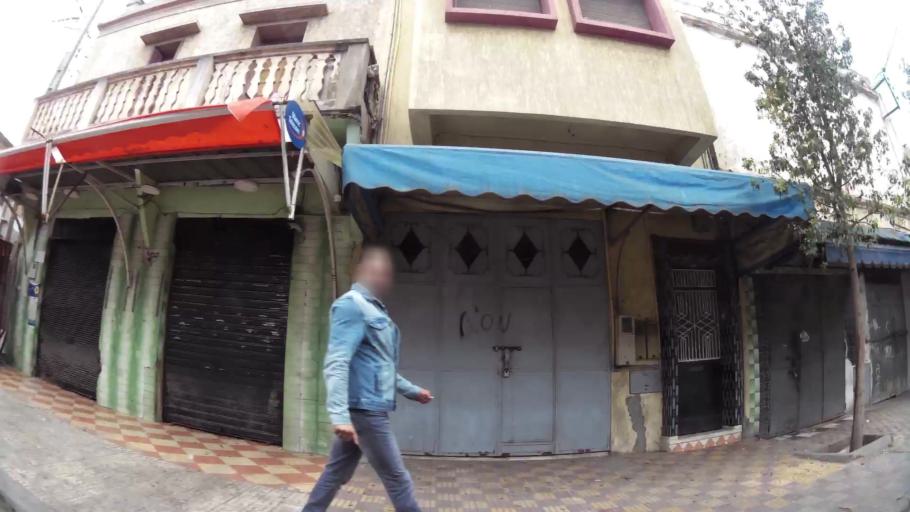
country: MA
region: Gharb-Chrarda-Beni Hssen
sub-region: Kenitra Province
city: Kenitra
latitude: 34.2625
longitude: -6.5688
